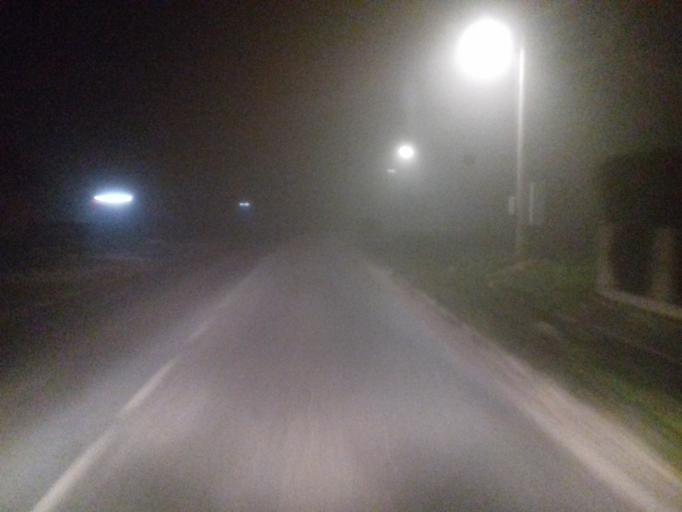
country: BA
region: Federation of Bosnia and Herzegovina
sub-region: Kanton Sarajevo
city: Sarajevo
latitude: 43.7900
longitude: 18.3609
